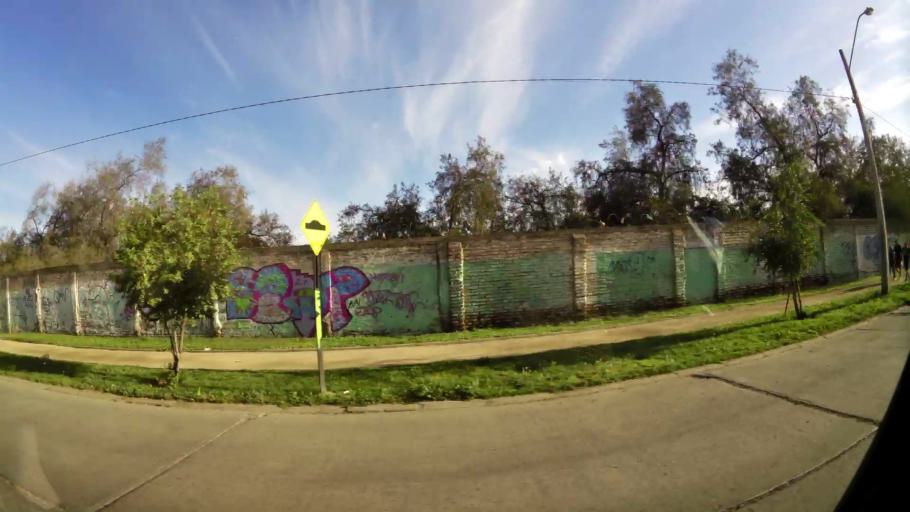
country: CL
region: Santiago Metropolitan
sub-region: Provincia de Santiago
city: Lo Prado
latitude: -33.4377
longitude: -70.7136
